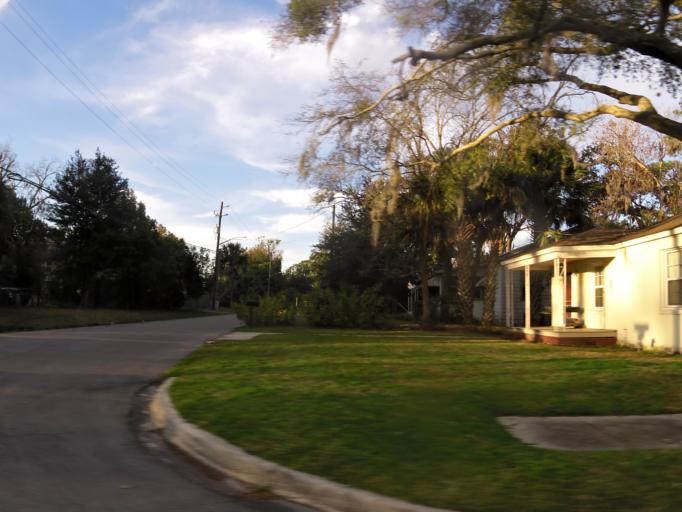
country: US
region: Florida
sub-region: Duval County
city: Jacksonville
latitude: 30.2904
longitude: -81.6422
